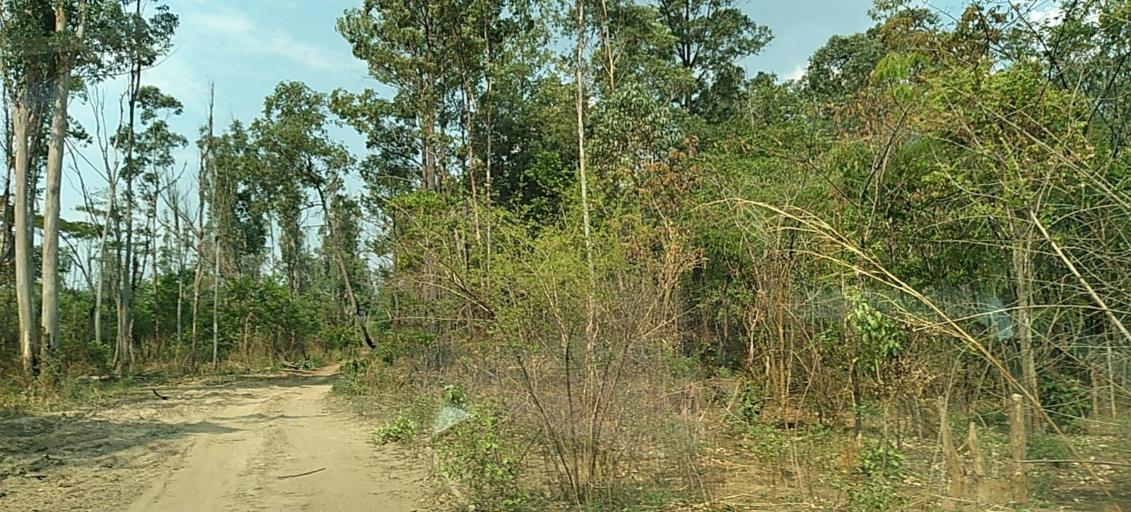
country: ZM
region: Copperbelt
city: Chingola
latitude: -12.7395
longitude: 27.7533
